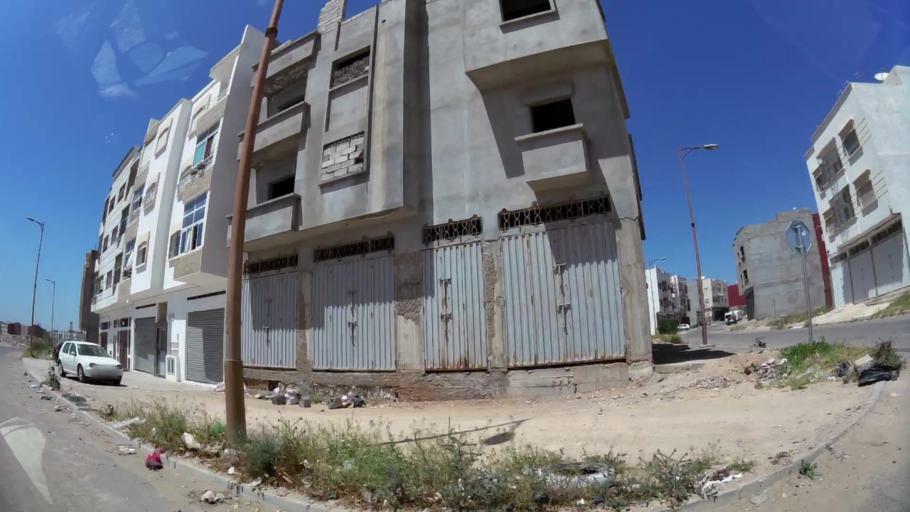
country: MA
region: Oued ed Dahab-Lagouira
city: Dakhla
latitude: 30.4306
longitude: -9.5498
